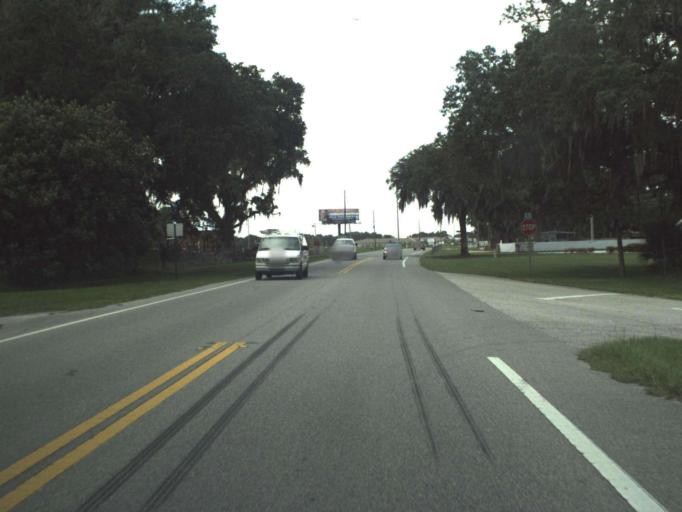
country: US
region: Florida
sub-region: Sumter County
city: Lake Panasoffkee
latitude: 28.7432
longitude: -82.0647
